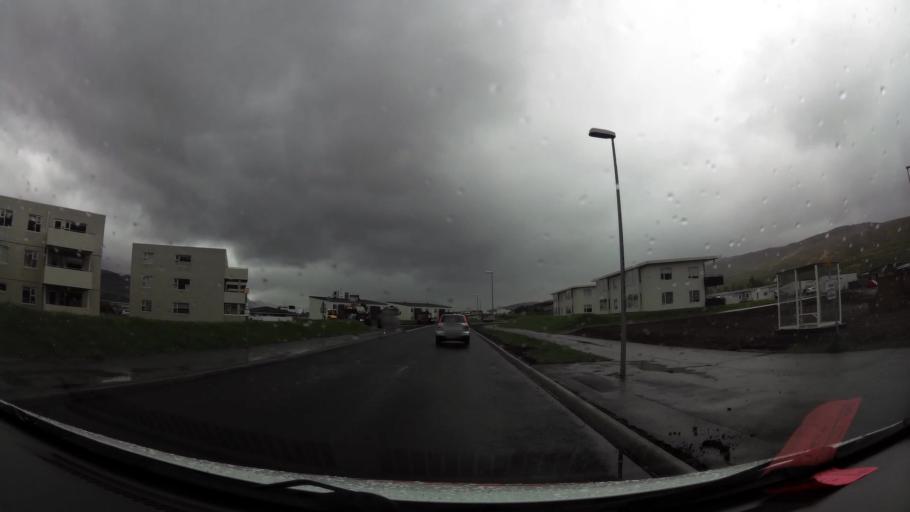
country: IS
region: Northeast
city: Akureyri
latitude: 65.6688
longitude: -18.1085
